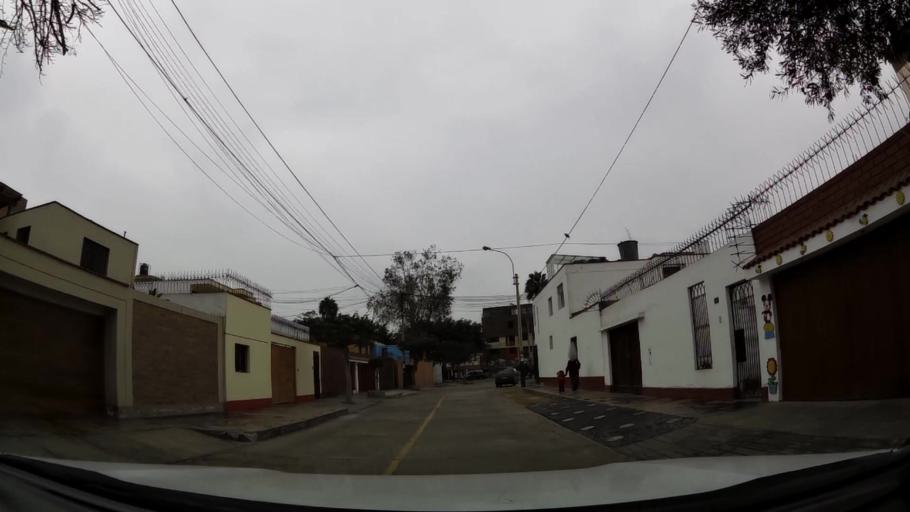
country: PE
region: Lima
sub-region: Lima
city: Surco
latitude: -12.1353
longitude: -77.0005
